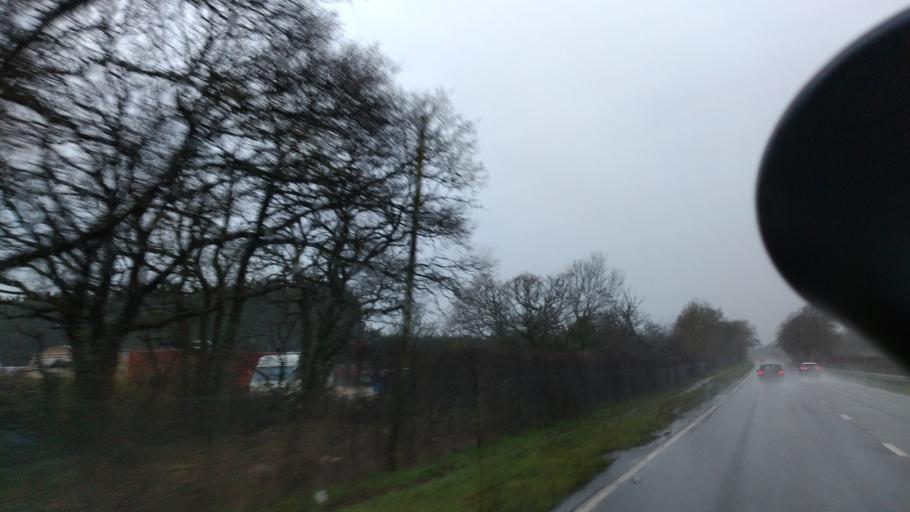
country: GB
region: England
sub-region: West Sussex
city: Rustington
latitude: 50.8419
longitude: -0.5080
